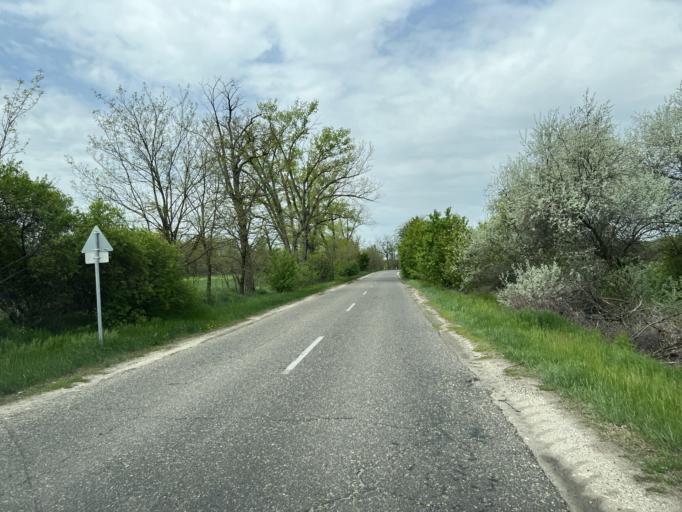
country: HU
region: Pest
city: Tortel
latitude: 47.1359
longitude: 19.8973
